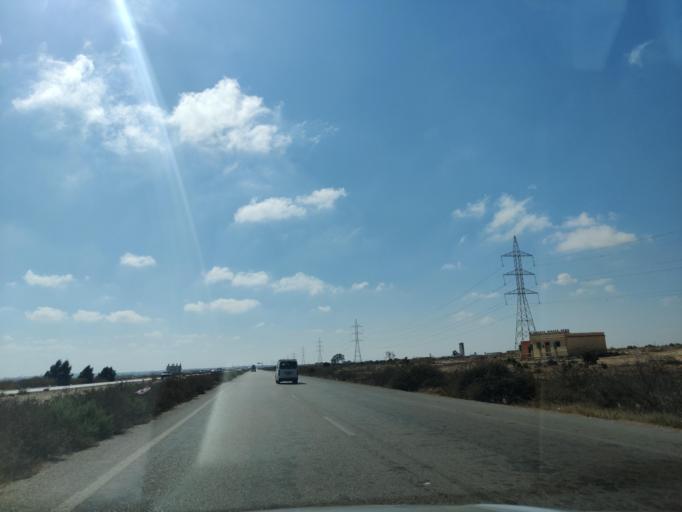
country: EG
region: Muhafazat Matruh
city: Al `Alamayn
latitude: 31.0517
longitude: 28.3219
